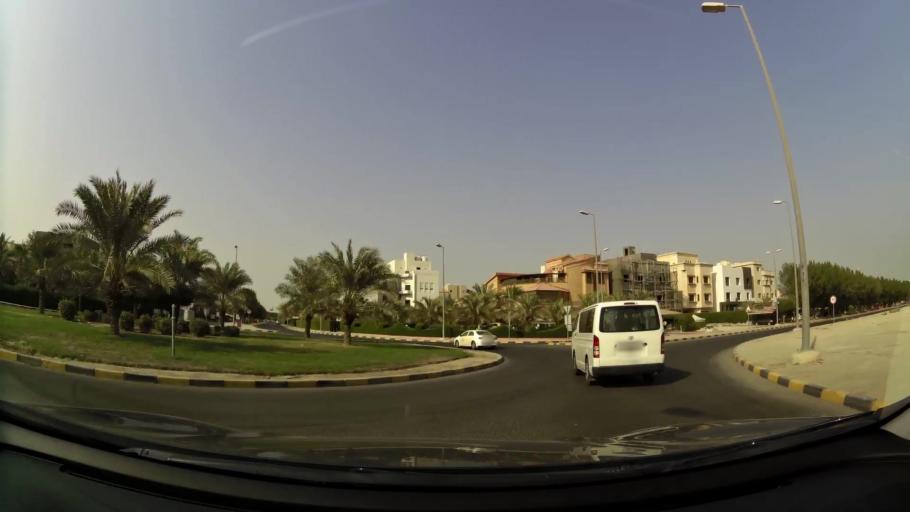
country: KW
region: Mubarak al Kabir
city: Sabah as Salim
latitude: 29.2772
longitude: 48.0438
